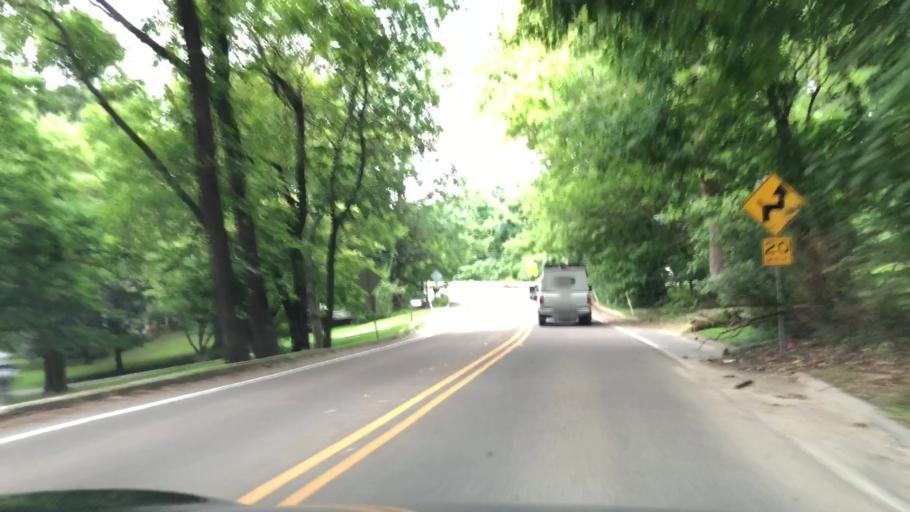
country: US
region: Pennsylvania
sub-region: Chester County
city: Devon
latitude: 40.0638
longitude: -75.4322
